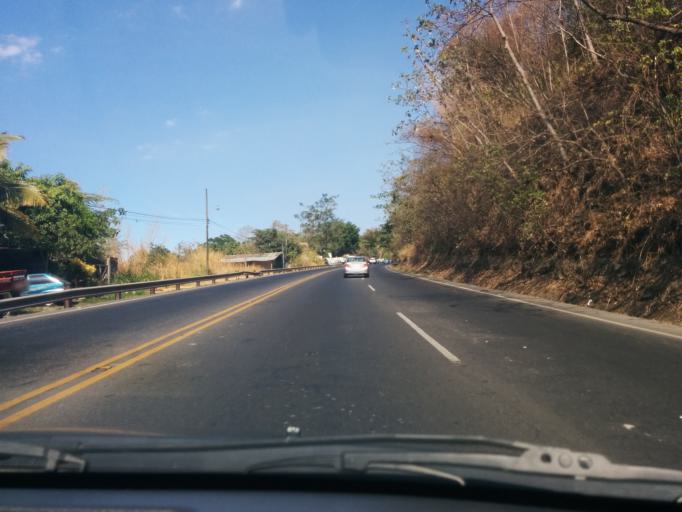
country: CR
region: Alajuela
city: Carrillos
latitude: 10.0031
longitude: -84.3063
